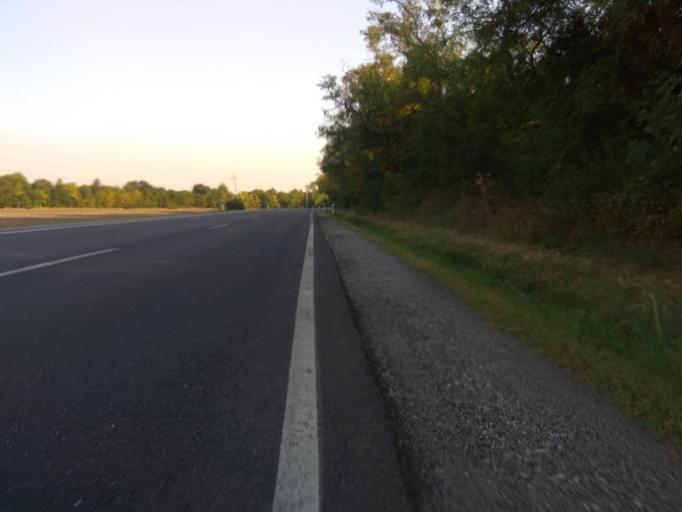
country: HU
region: Borsod-Abauj-Zemplen
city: Nyekladhaza
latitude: 47.9637
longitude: 20.8336
